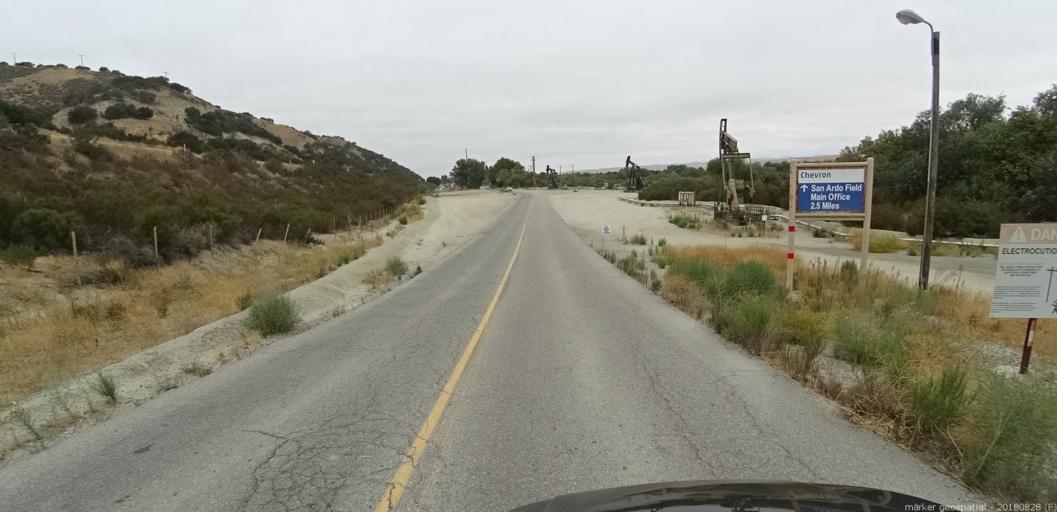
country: US
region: California
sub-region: San Luis Obispo County
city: Lake Nacimiento
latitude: 35.9488
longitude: -120.8761
